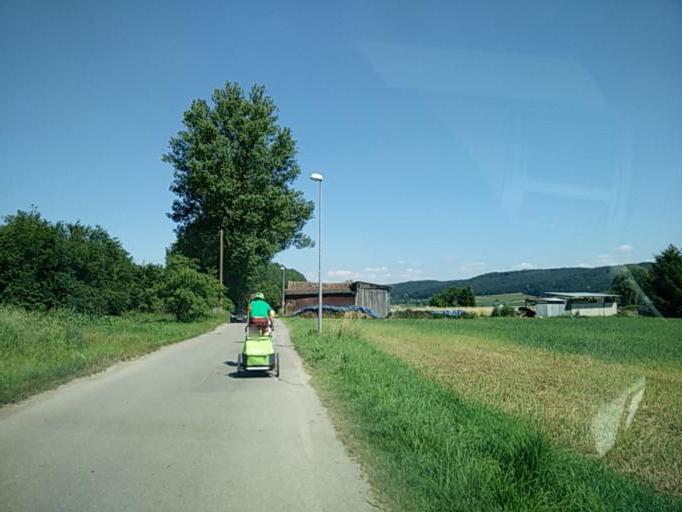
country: DE
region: Baden-Wuerttemberg
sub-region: Tuebingen Region
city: Rottenburg
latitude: 48.5234
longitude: 8.9775
